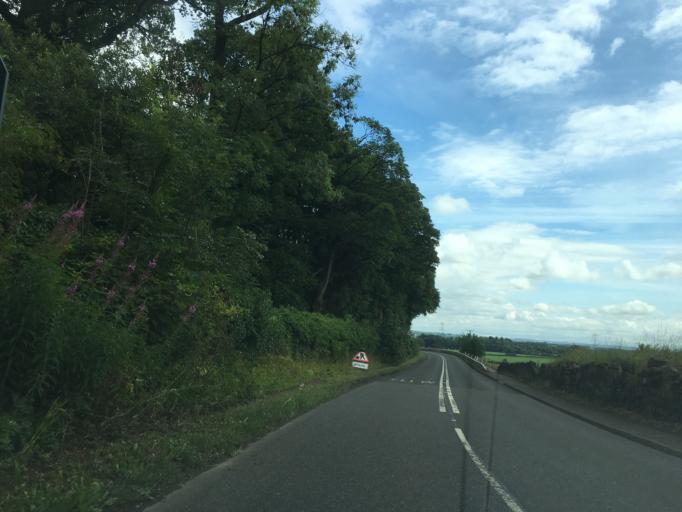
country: GB
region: Scotland
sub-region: Stirling
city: Stirling
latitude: 56.1417
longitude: -3.9137
